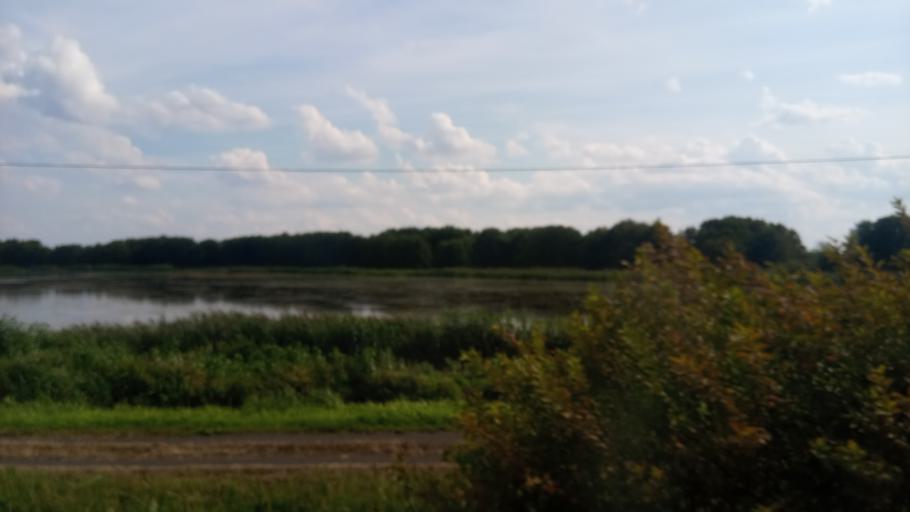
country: PL
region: Greater Poland Voivodeship
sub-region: Powiat pilski
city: Osiek nad Notecia
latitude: 53.1211
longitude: 17.3266
